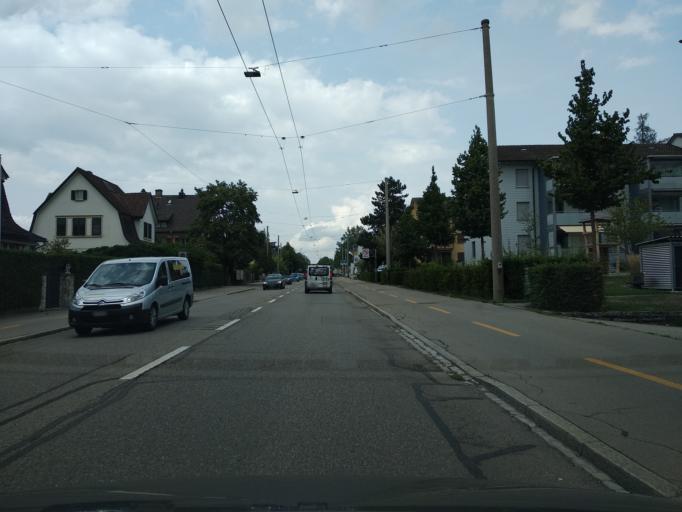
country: CH
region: Zurich
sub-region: Bezirk Winterthur
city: Veltheim
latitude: 47.5149
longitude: 8.7211
